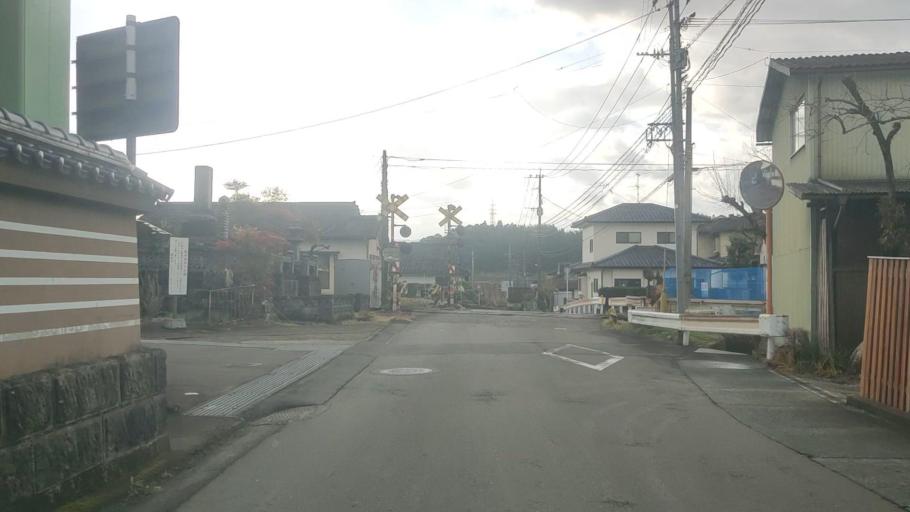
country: JP
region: Kumamoto
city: Hitoyoshi
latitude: 32.2179
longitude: 130.7718
